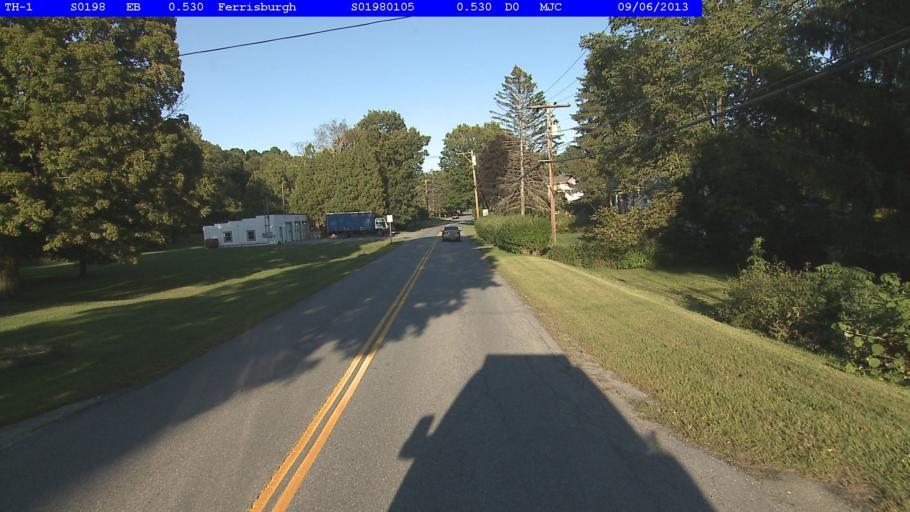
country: US
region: Vermont
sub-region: Addison County
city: Vergennes
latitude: 44.2589
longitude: -73.2175
